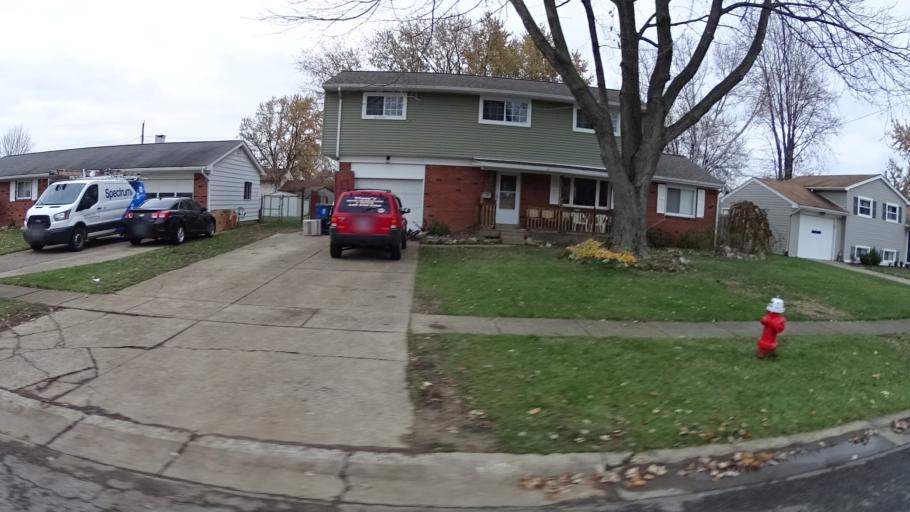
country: US
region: Ohio
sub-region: Lorain County
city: Lorain
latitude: 41.4324
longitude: -82.2037
